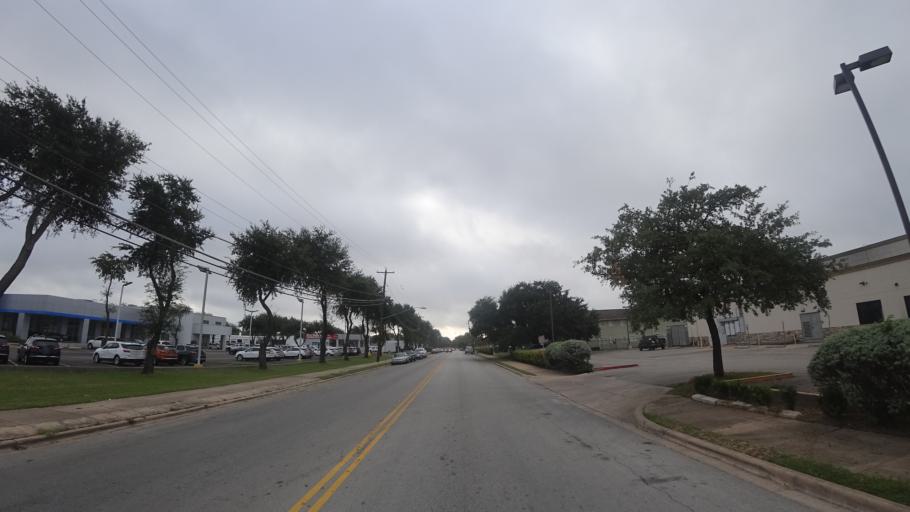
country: US
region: Texas
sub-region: Travis County
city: Wells Branch
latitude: 30.3508
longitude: -97.6920
